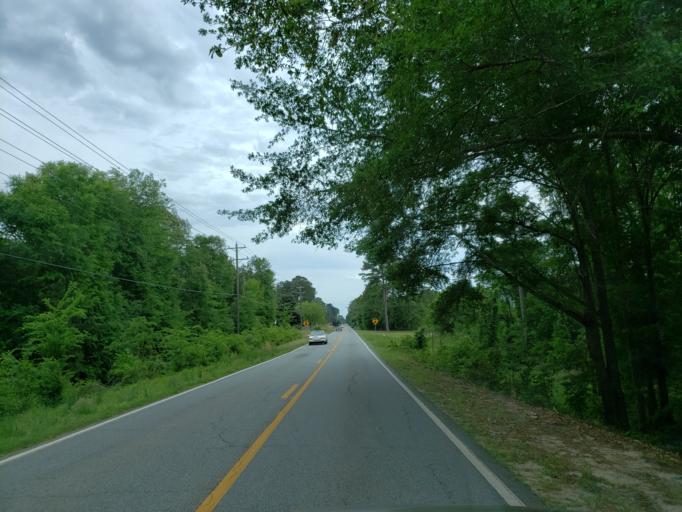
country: US
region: Georgia
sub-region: Bibb County
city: West Point
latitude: 32.7735
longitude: -83.7799
